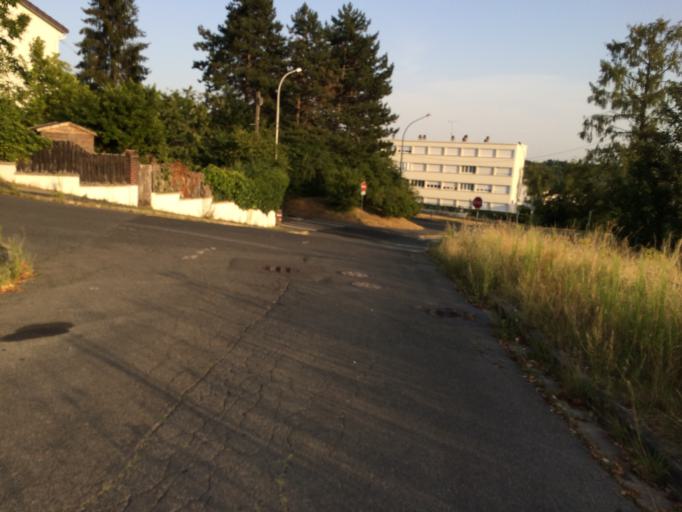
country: FR
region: Ile-de-France
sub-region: Departement de l'Essonne
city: Verrieres-le-Buisson
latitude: 48.7417
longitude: 2.2512
